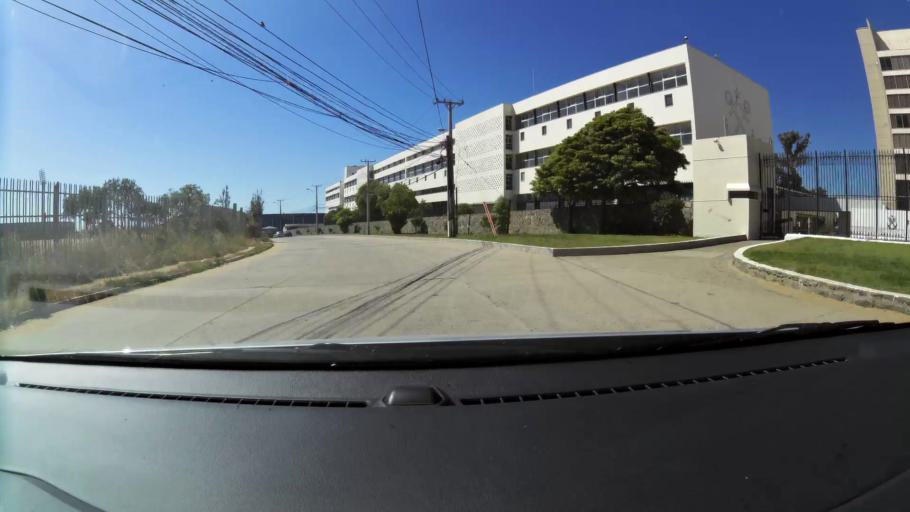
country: CL
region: Valparaiso
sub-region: Provincia de Valparaiso
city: Valparaiso
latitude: -33.0222
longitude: -71.6373
